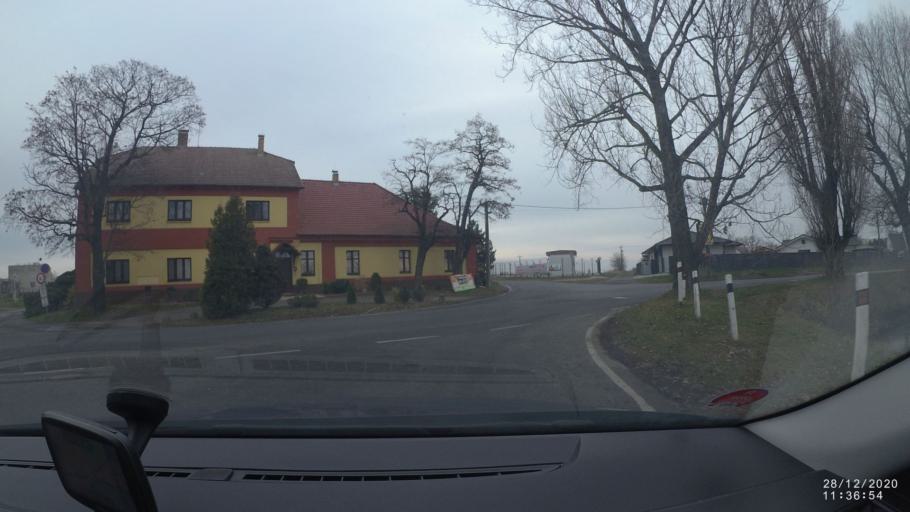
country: CZ
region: Praha
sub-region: Praha 20
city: Horni Pocernice
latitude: 50.1395
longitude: 14.6149
